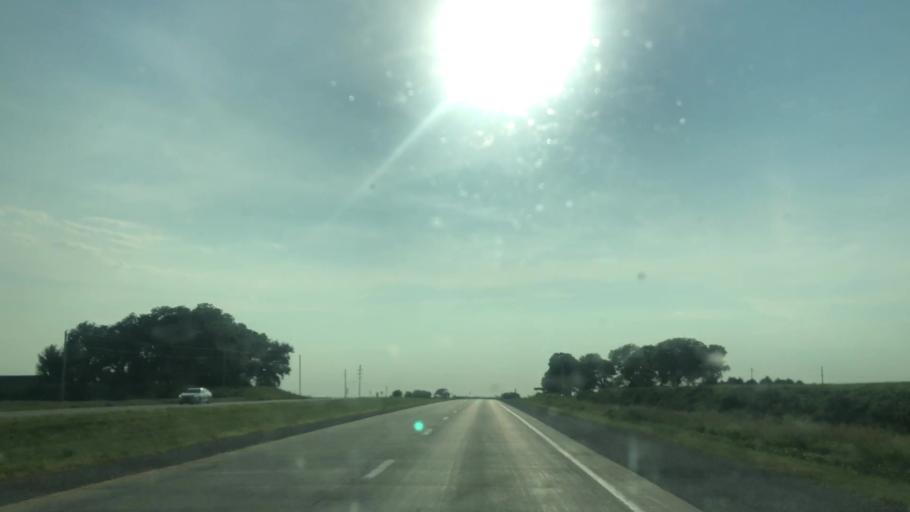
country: US
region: Iowa
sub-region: Story County
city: Nevada
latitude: 42.0079
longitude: -93.4016
